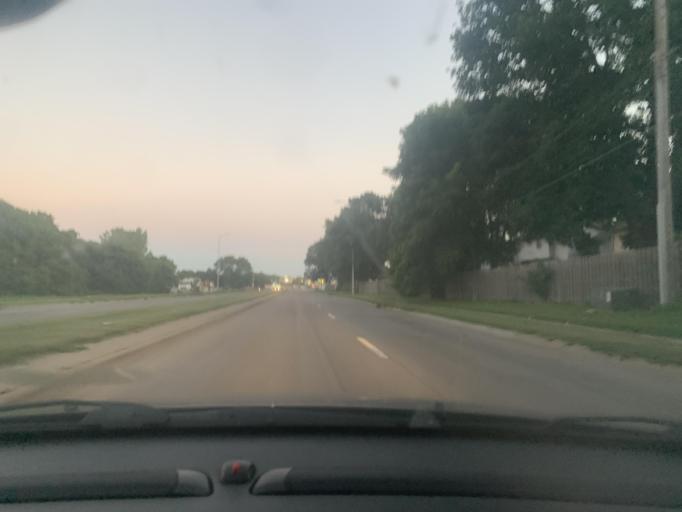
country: US
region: Nebraska
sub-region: Douglas County
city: Ralston
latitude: 41.2972
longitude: -96.0527
